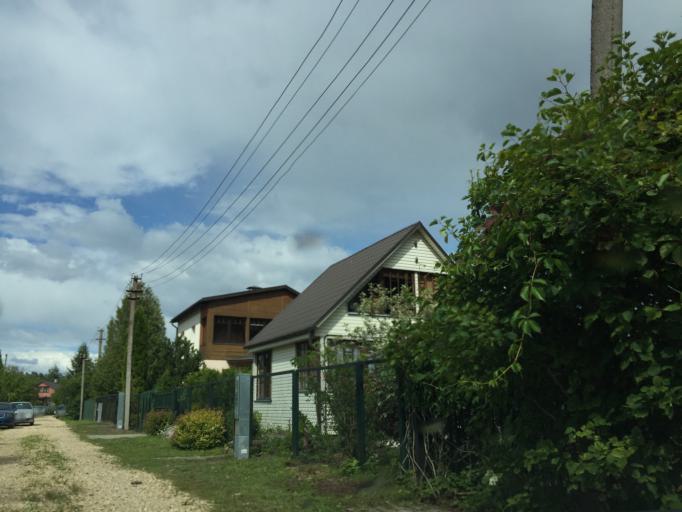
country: LV
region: Carnikava
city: Carnikava
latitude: 57.1170
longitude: 24.2239
